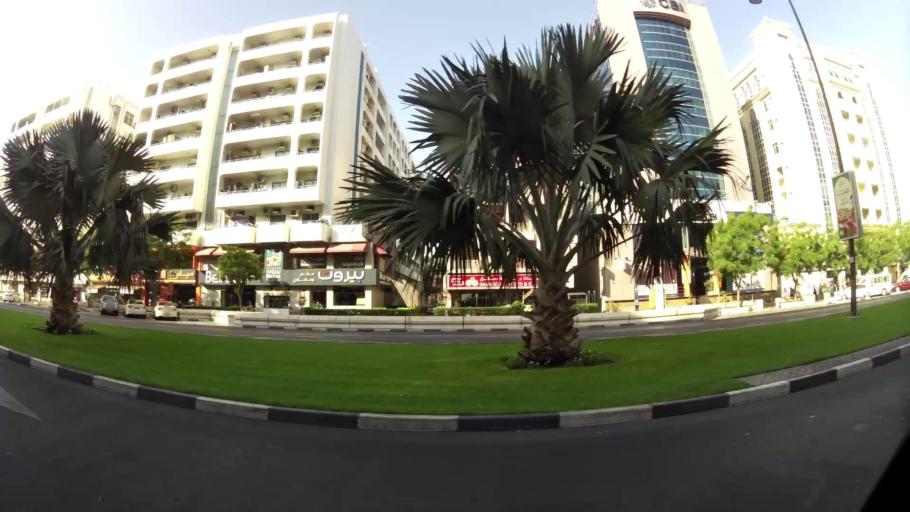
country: AE
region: Ash Shariqah
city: Sharjah
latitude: 25.2652
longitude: 55.3202
